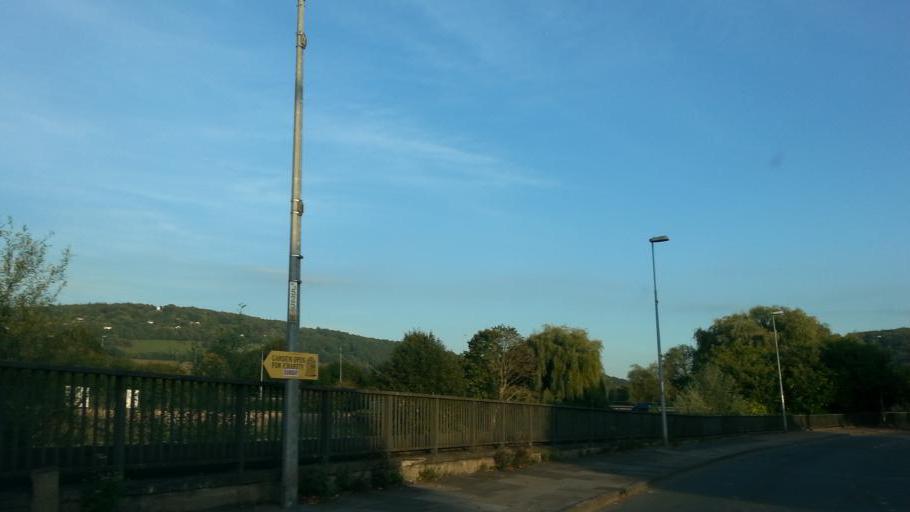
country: GB
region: Wales
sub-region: Monmouthshire
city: Monmouth
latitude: 51.8065
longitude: -2.7174
